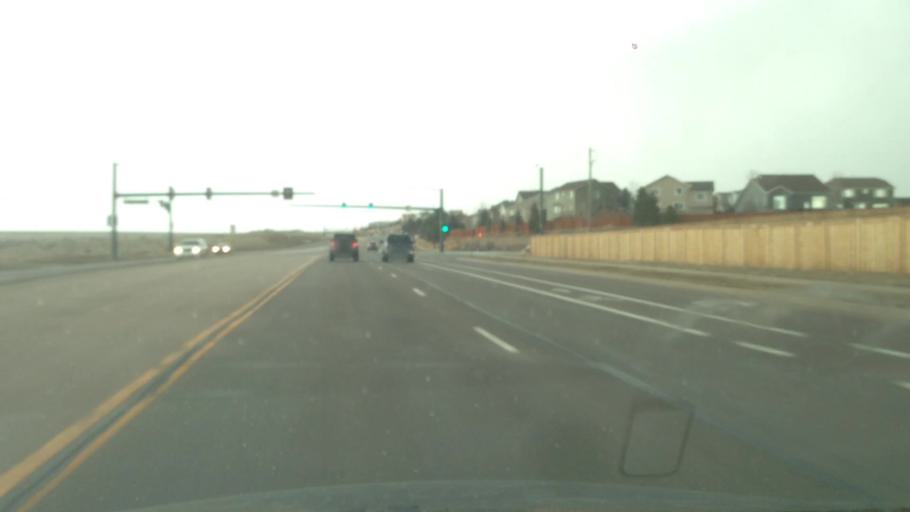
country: US
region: Colorado
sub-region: Douglas County
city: Stonegate
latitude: 39.4930
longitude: -104.7924
